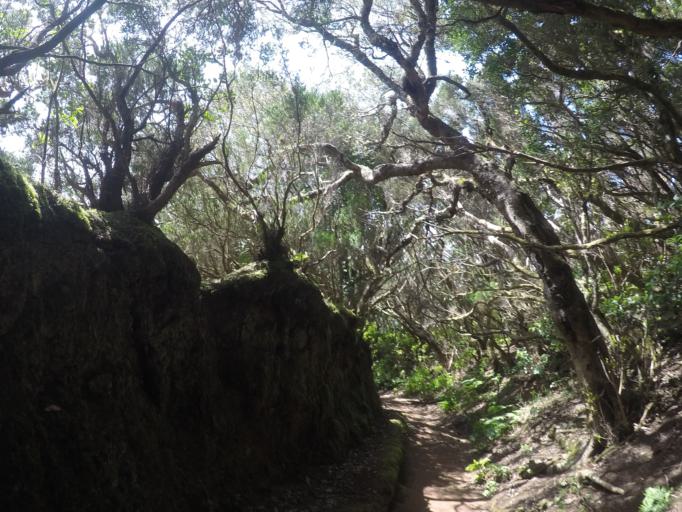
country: ES
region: Canary Islands
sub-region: Provincia de Santa Cruz de Tenerife
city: Santa Cruz de Tenerife
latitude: 28.5421
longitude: -16.2286
